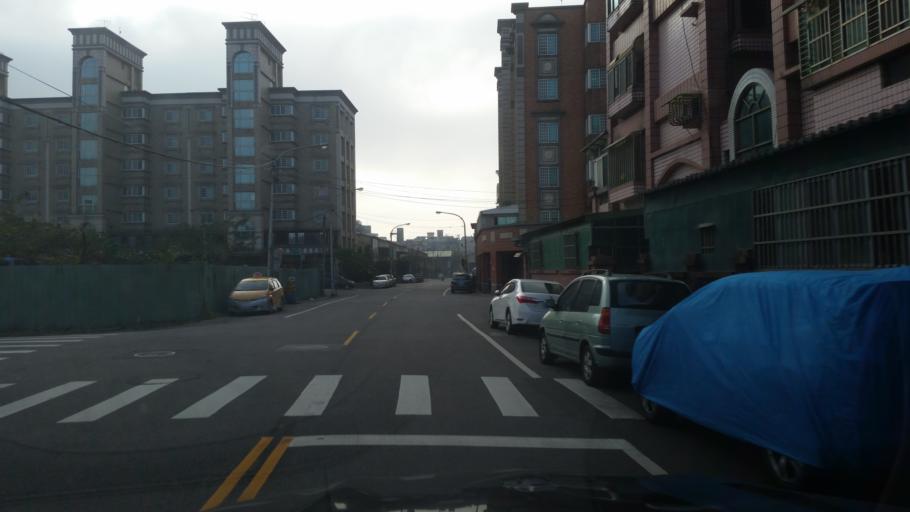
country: TW
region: Taiwan
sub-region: Taoyuan
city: Taoyuan
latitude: 25.0569
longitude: 121.3589
